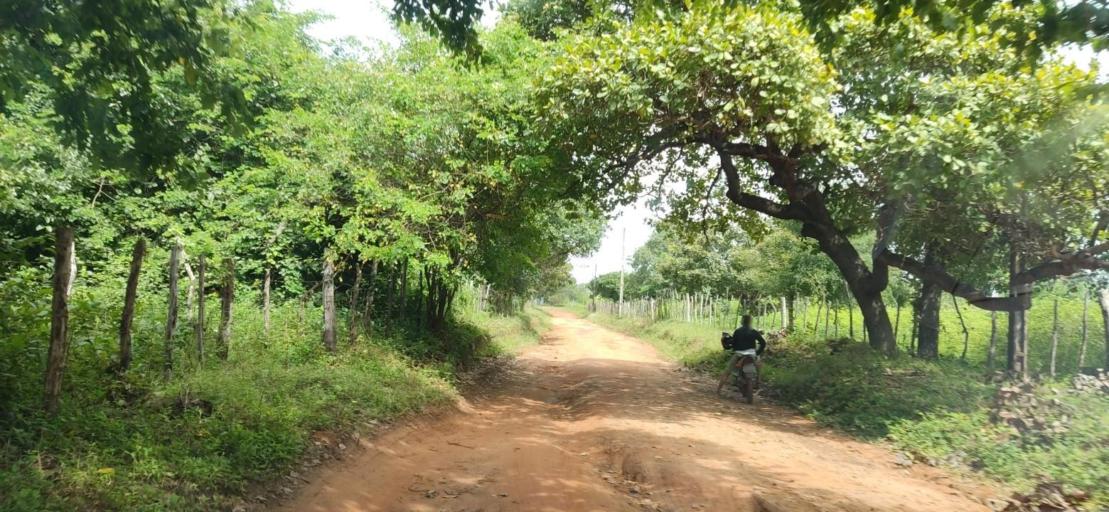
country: BR
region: Piaui
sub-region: Valenca Do Piaui
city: Valenca do Piaui
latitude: -6.1098
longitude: -41.8032
